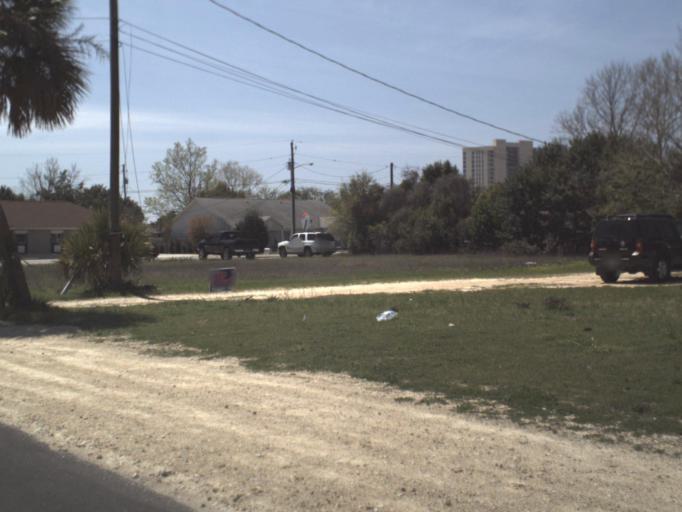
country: US
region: Florida
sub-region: Bay County
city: Laguna Beach
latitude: 30.2274
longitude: -85.8890
